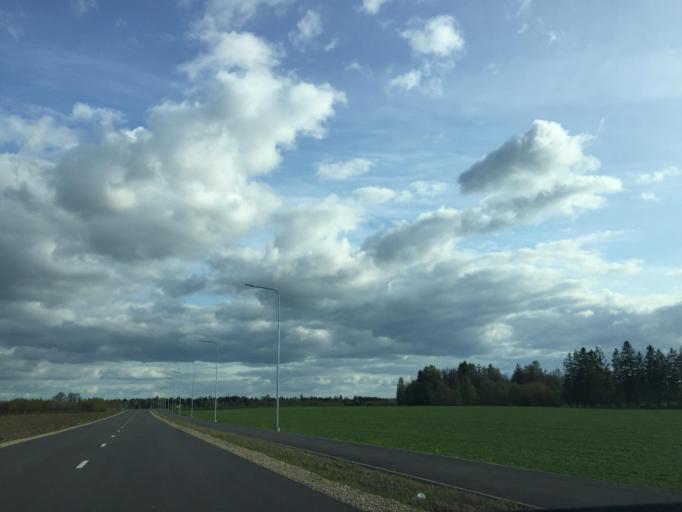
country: LV
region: Sigulda
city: Sigulda
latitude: 57.1393
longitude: 24.8611
